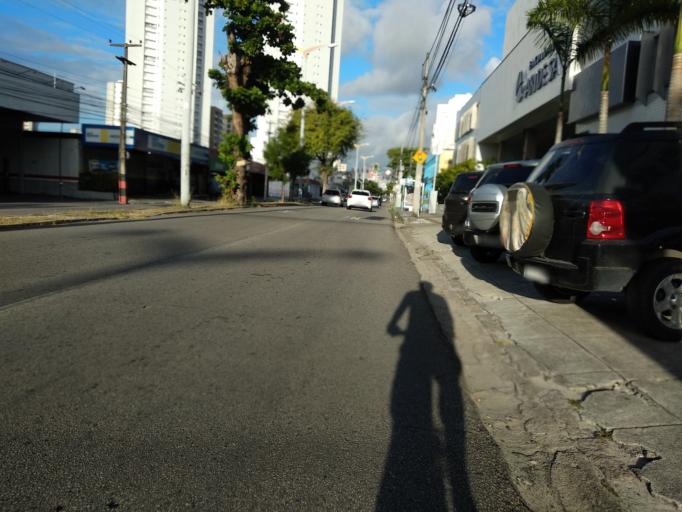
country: BR
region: Ceara
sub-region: Fortaleza
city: Fortaleza
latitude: -3.7359
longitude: -38.5175
